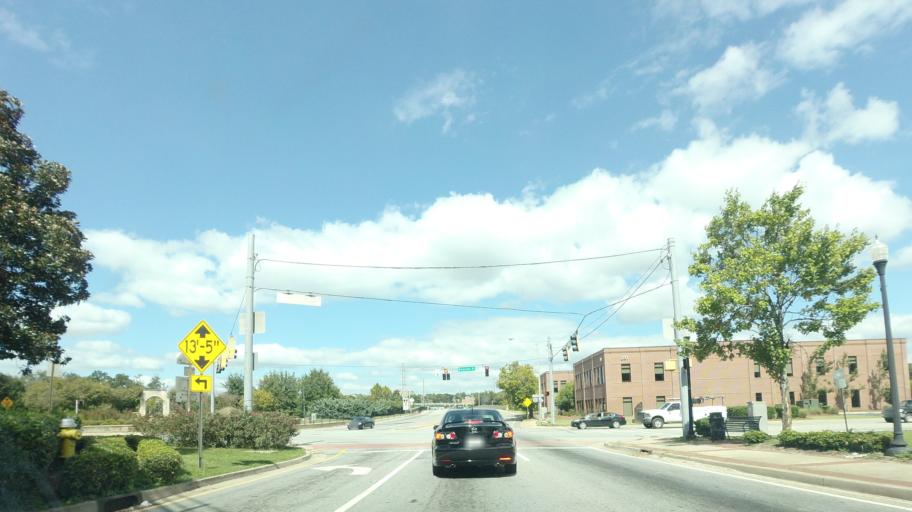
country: US
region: Georgia
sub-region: Bibb County
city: Macon
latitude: 32.8375
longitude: -83.6213
